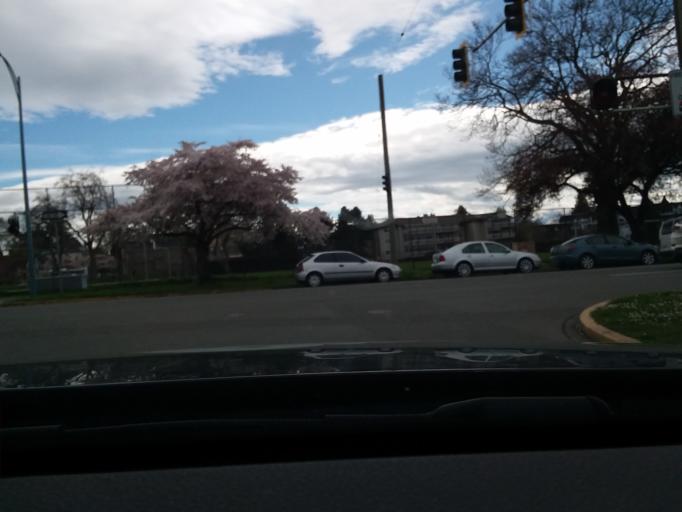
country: CA
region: British Columbia
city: Victoria
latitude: 48.4248
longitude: -123.3474
